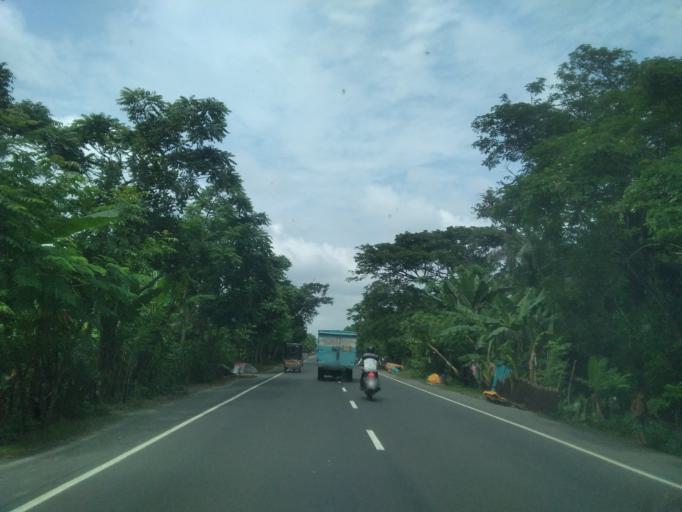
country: BD
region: Khulna
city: Kesabpur
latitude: 22.7951
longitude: 89.2254
